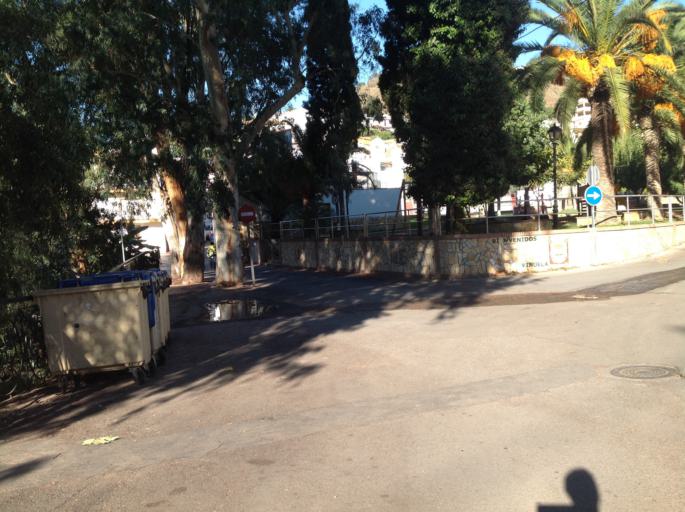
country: ES
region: Andalusia
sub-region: Provincia de Malaga
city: Vinuela
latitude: 36.8613
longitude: -4.1398
